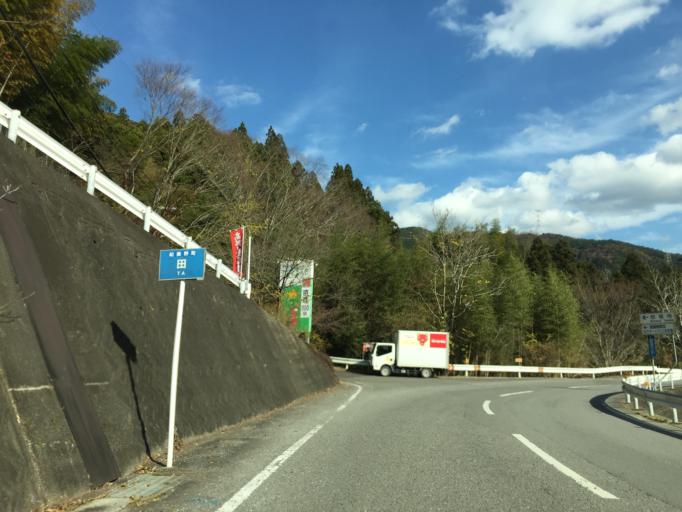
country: JP
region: Wakayama
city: Iwade
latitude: 34.1397
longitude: 135.4136
